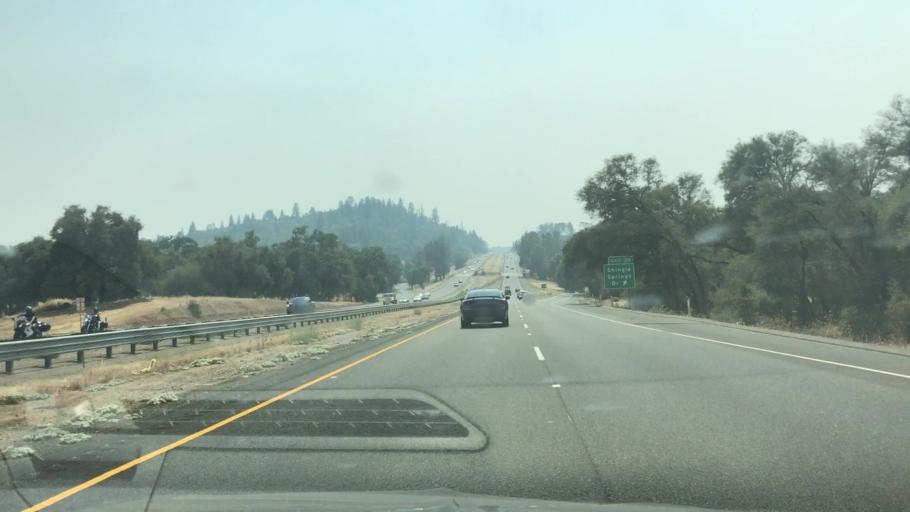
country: US
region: California
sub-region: El Dorado County
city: Shingle Springs
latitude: 38.6840
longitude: -120.9115
